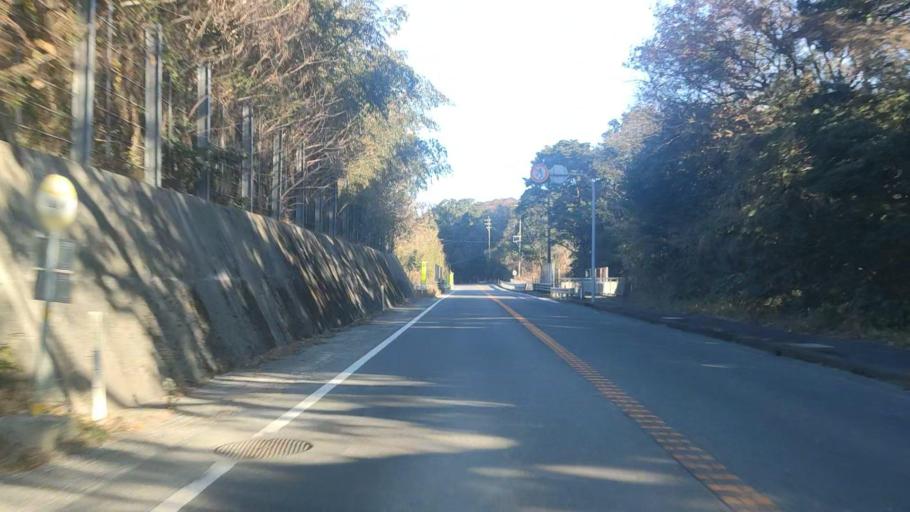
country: JP
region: Miyazaki
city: Nobeoka
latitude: 32.3497
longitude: 131.6229
